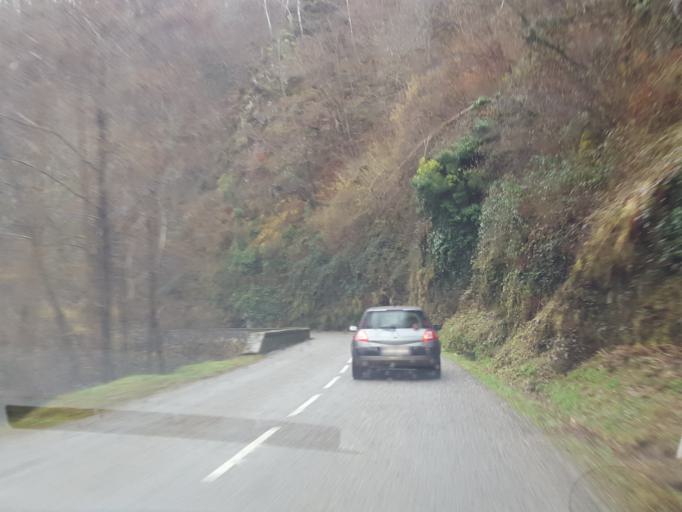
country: FR
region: Midi-Pyrenees
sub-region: Departement de l'Ariege
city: Saint-Girons
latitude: 42.9137
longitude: 1.2625
